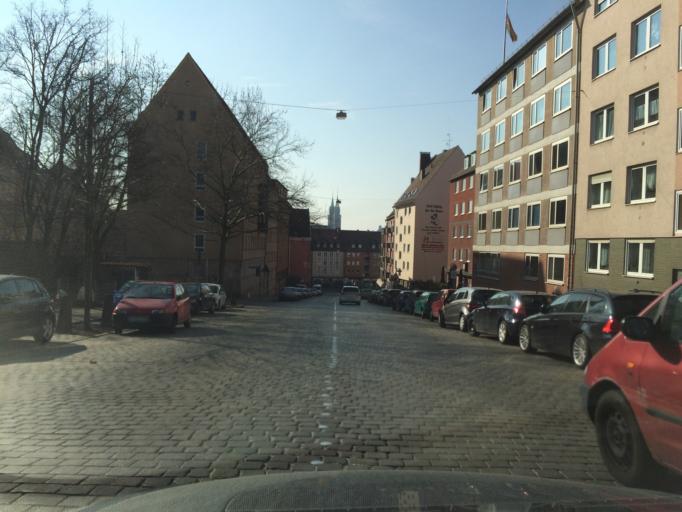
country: DE
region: Bavaria
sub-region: Regierungsbezirk Mittelfranken
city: Nuernberg
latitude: 49.4574
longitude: 11.0803
